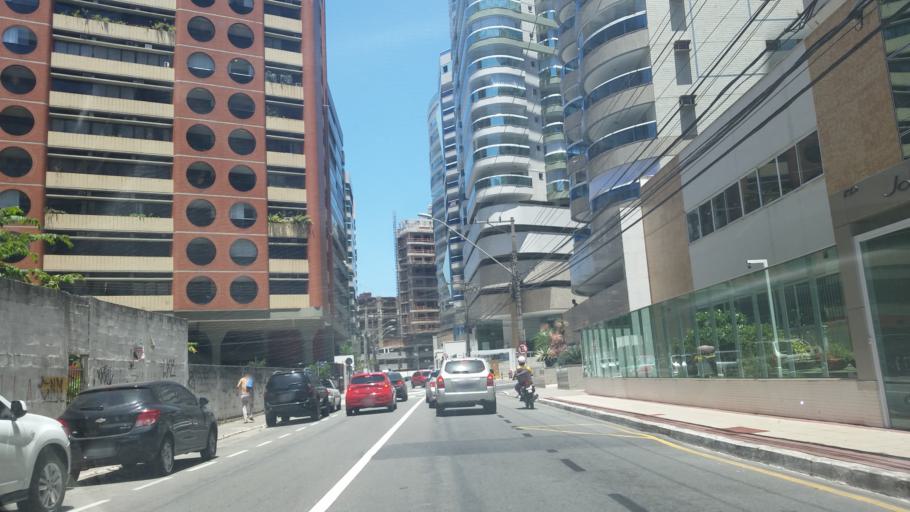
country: BR
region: Espirito Santo
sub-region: Vila Velha
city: Vila Velha
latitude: -20.3343
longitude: -40.2812
